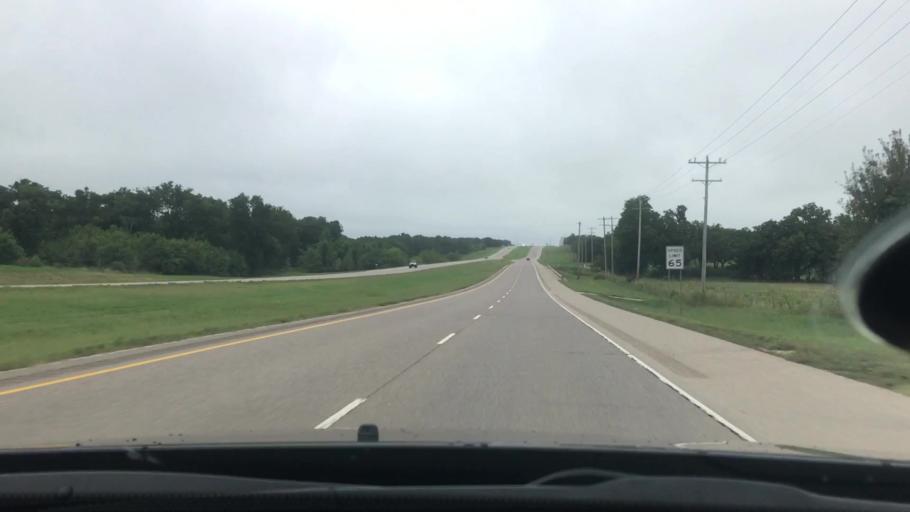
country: US
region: Oklahoma
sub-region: Seminole County
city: Seminole
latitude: 35.3354
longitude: -96.6713
